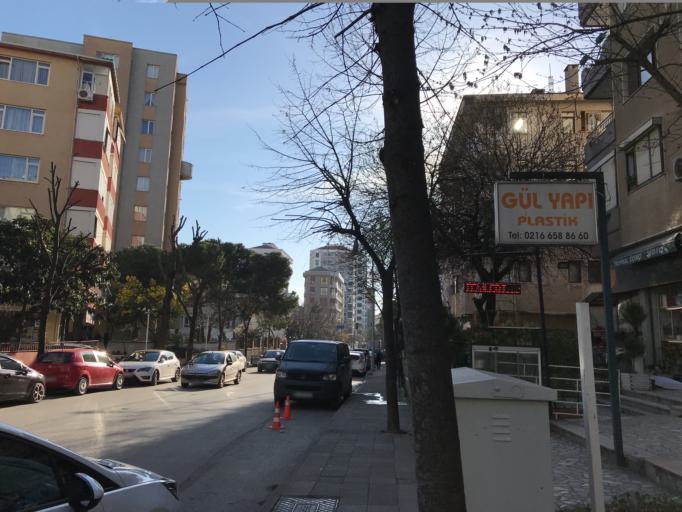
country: TR
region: Istanbul
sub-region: Atasehir
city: Atasehir
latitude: 40.9639
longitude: 29.0996
